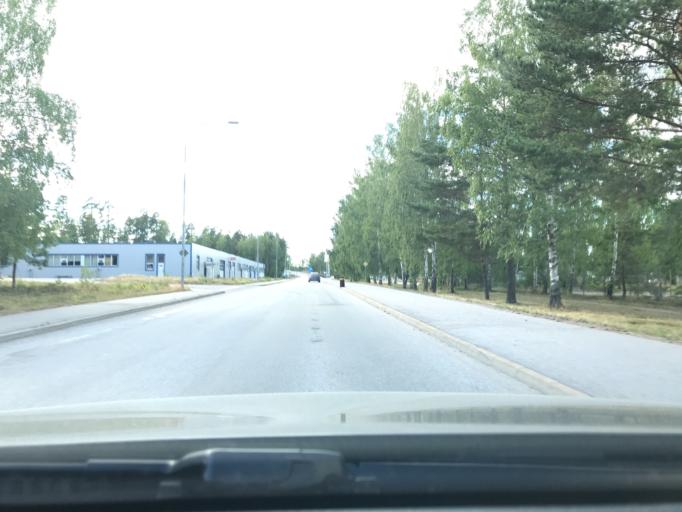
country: SE
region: Kalmar
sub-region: Hultsfreds Kommun
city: Hultsfred
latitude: 57.4977
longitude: 15.8292
